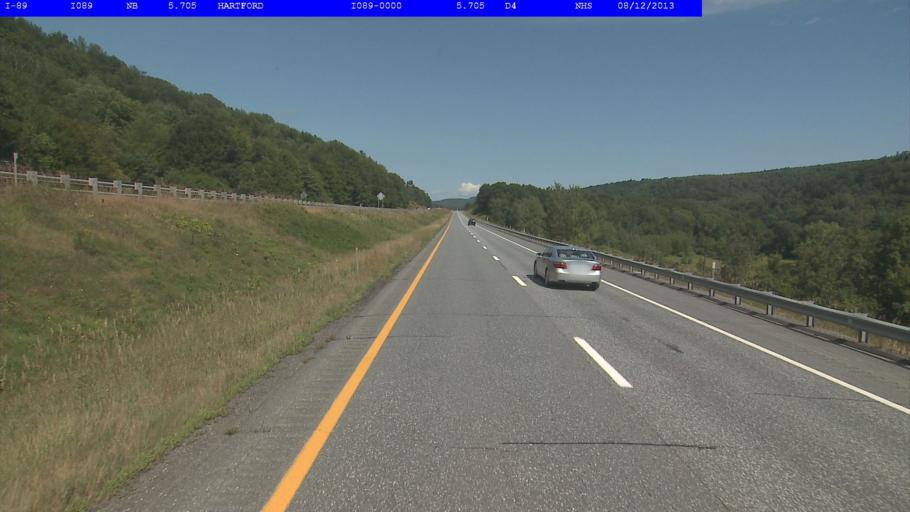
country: US
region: Vermont
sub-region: Windsor County
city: White River Junction
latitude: 43.6883
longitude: -72.4038
